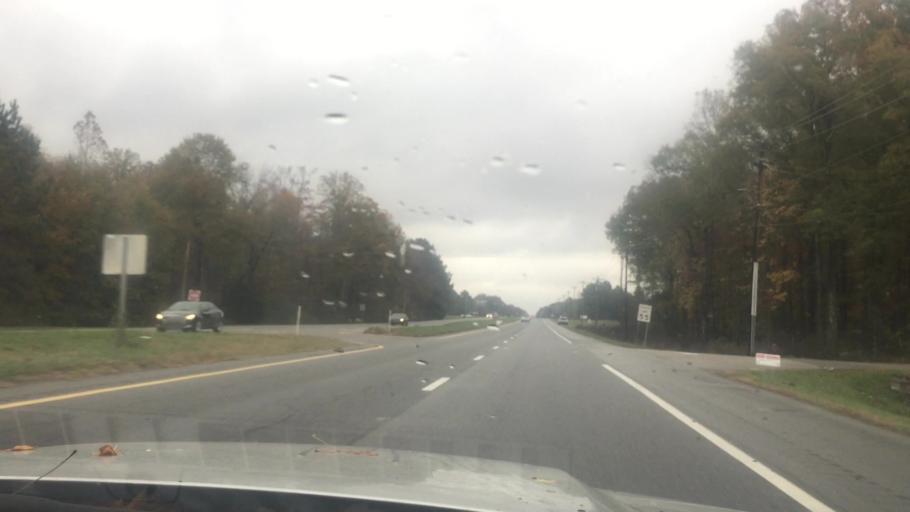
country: US
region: Tennessee
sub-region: Coffee County
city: Tullahoma
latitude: 35.3710
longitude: -86.1837
